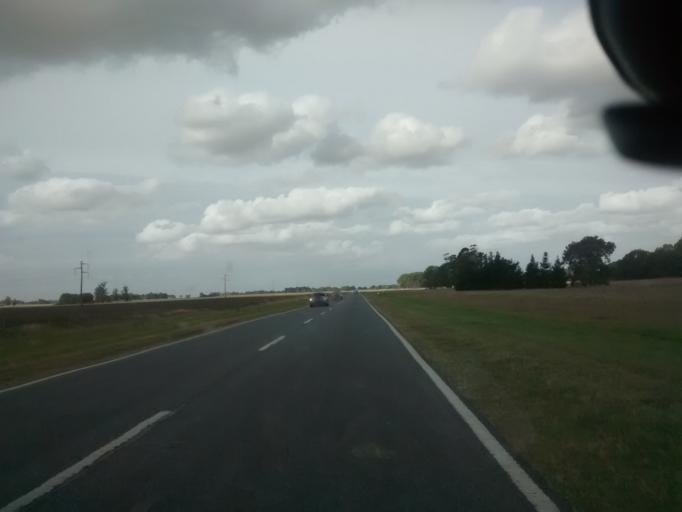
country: AR
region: Buenos Aires
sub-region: Partido de Balcarce
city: Balcarce
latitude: -37.6708
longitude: -58.4941
